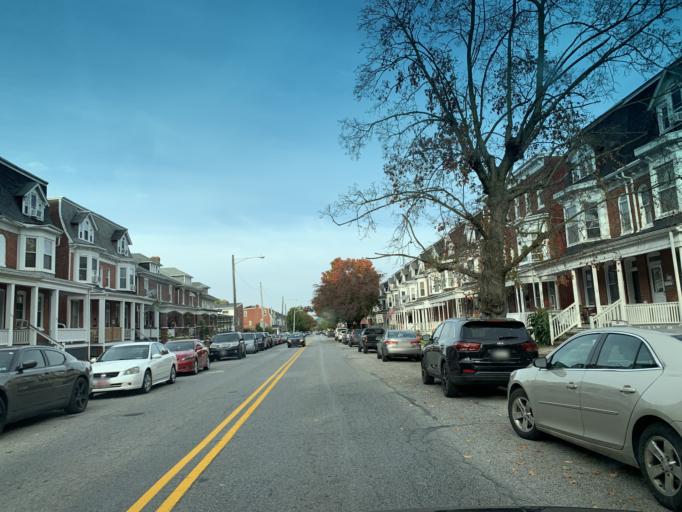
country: US
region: Pennsylvania
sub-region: York County
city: West York
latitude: 39.9619
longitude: -76.7497
